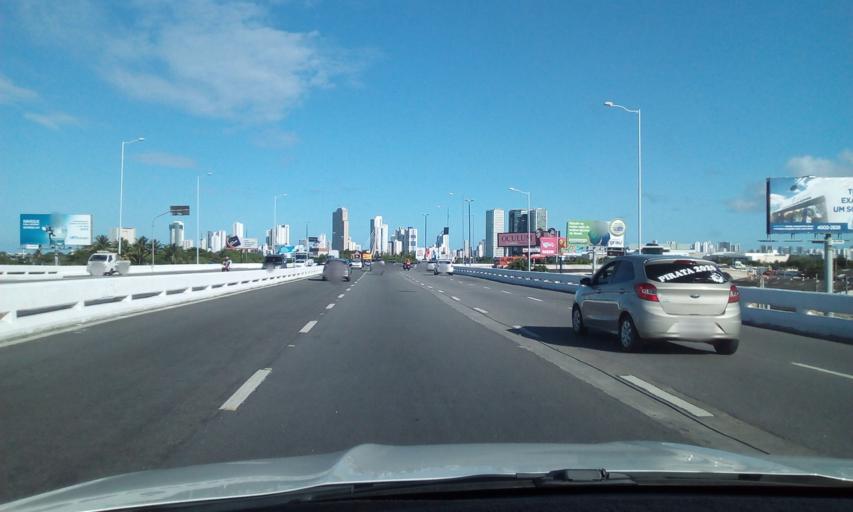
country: BR
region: Pernambuco
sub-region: Recife
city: Recife
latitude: -8.0744
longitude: -34.8936
